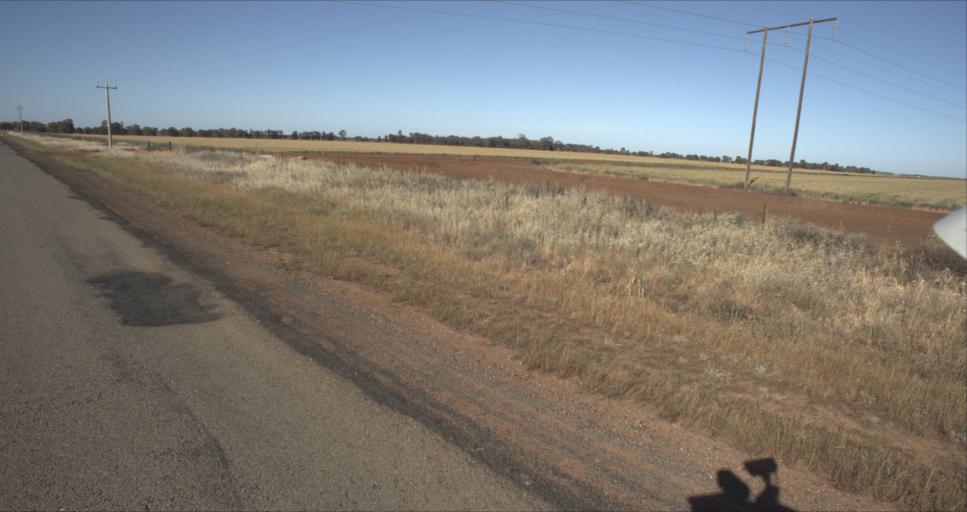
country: AU
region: New South Wales
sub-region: Leeton
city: Leeton
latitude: -34.5596
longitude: 146.2657
